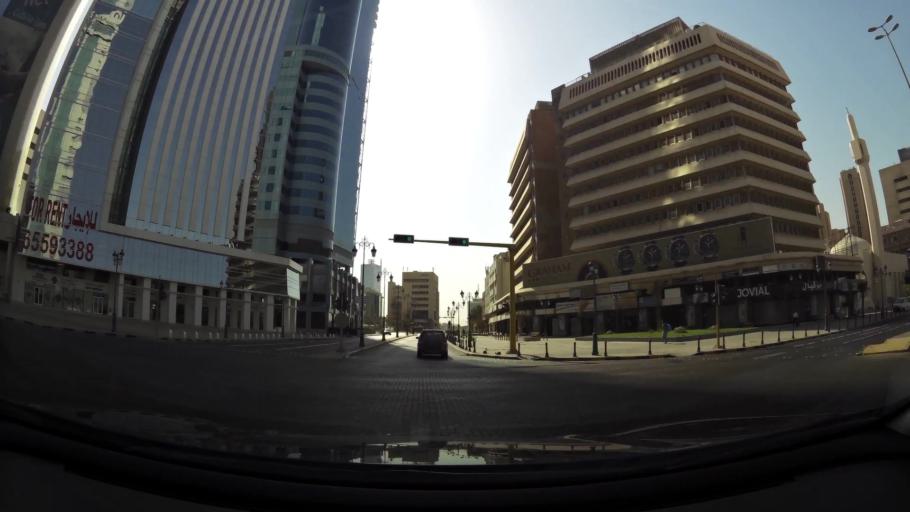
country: KW
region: Al Asimah
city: Kuwait City
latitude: 29.3689
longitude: 47.9692
